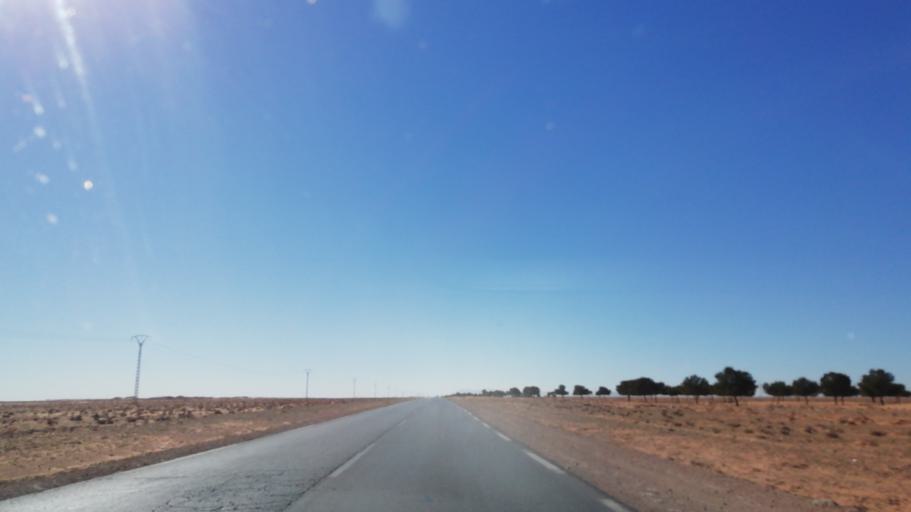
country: DZ
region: Saida
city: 'Ain el Hadjar
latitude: 33.9816
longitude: 0.0290
